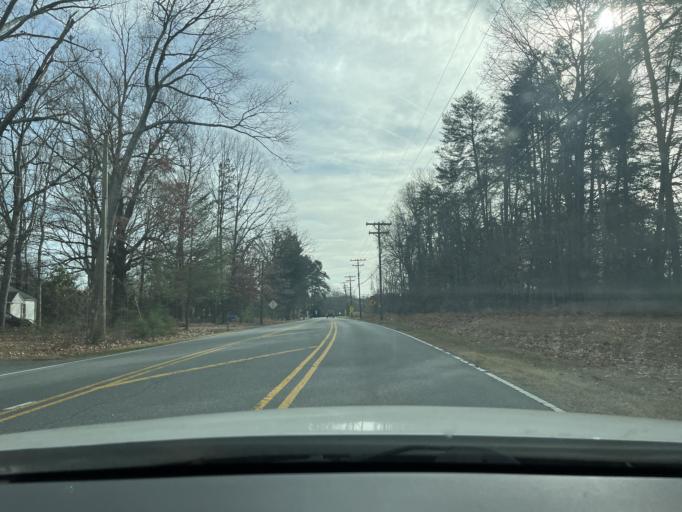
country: US
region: North Carolina
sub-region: Guilford County
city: Pleasant Garden
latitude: 36.0157
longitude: -79.7763
